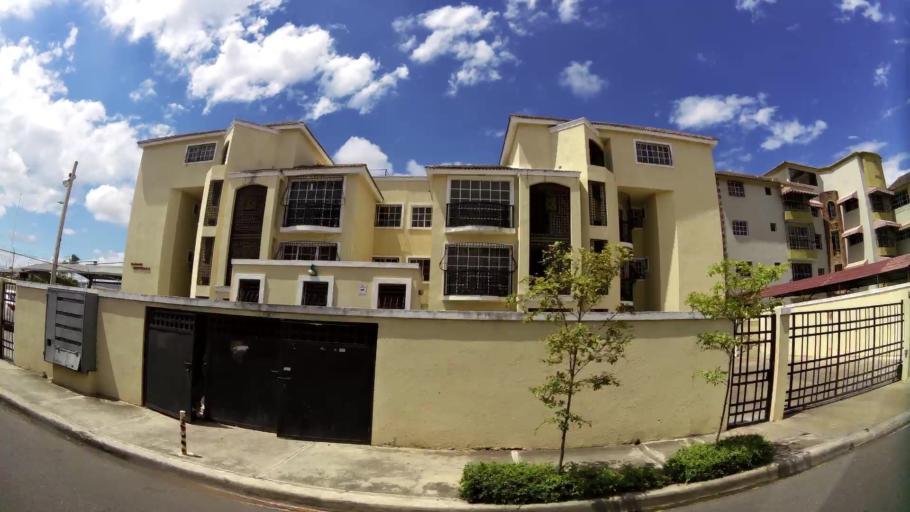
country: DO
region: Santiago
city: Santiago de los Caballeros
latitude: 19.4562
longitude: -70.6623
